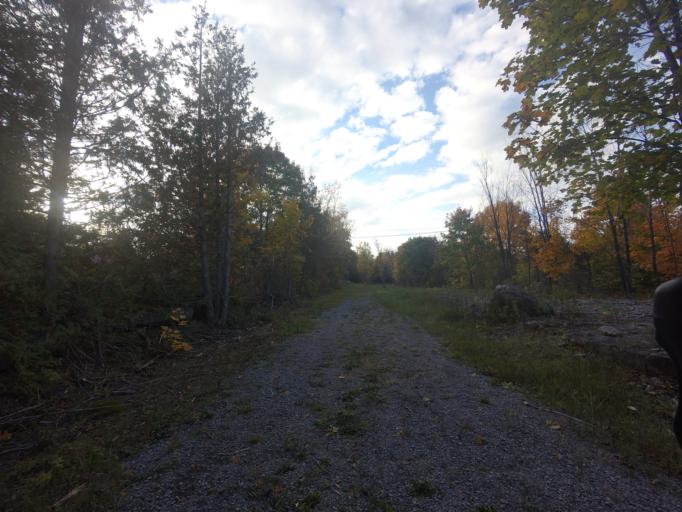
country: CA
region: Ontario
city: Pembroke
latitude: 45.5337
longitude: -77.0916
